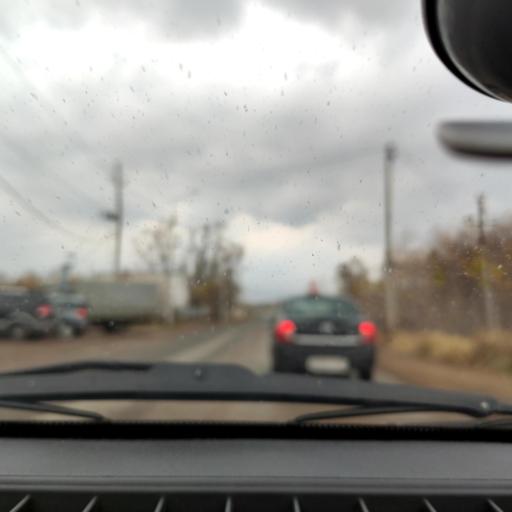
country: RU
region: Bashkortostan
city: Ufa
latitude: 54.7688
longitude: 55.9585
